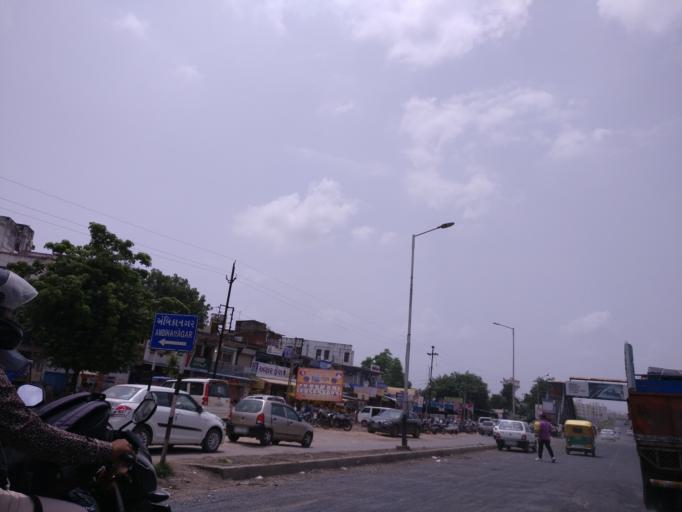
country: IN
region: Gujarat
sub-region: Mahesana
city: Jhulasan
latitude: 23.2386
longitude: 72.4920
